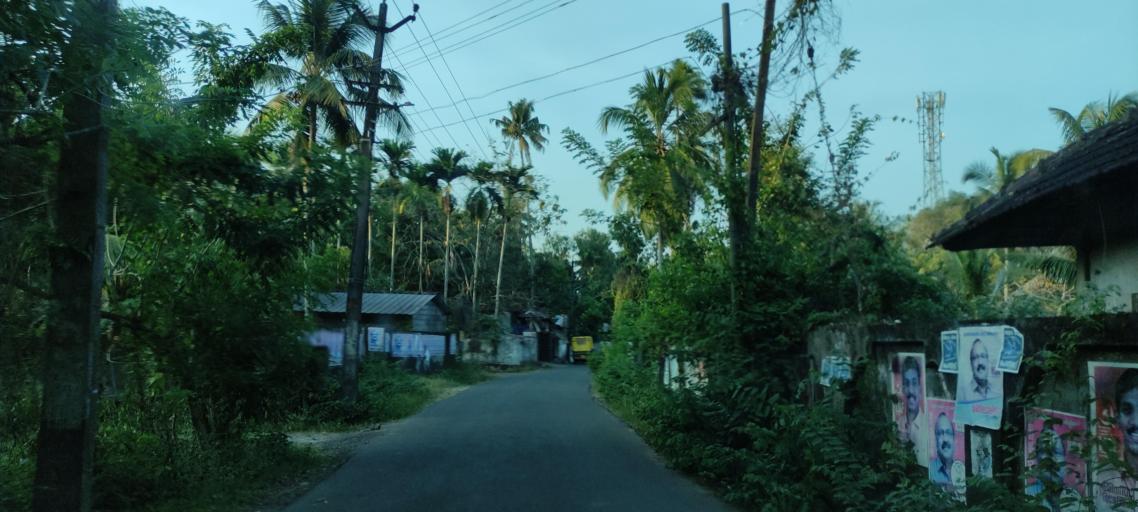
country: IN
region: Kerala
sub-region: Alappuzha
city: Kutiatodu
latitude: 9.7785
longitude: 76.3249
